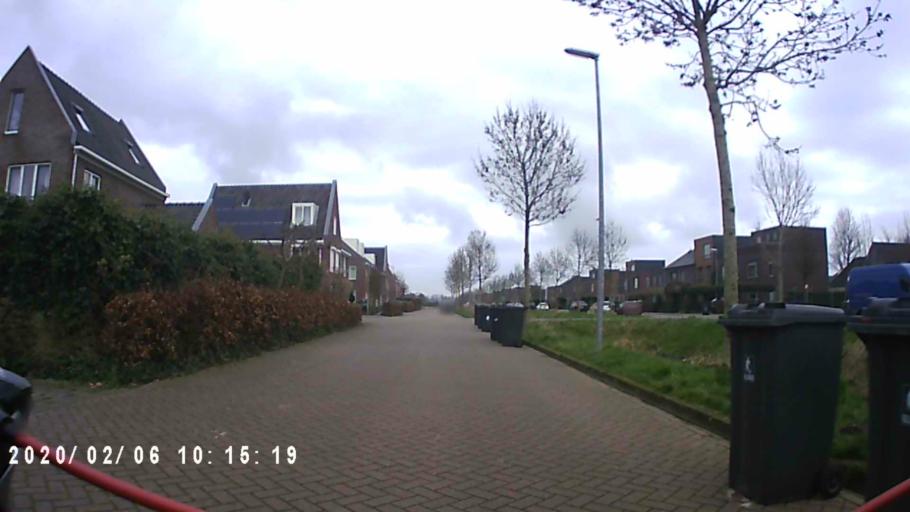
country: NL
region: Groningen
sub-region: Gemeente Groningen
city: Korrewegwijk
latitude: 53.2409
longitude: 6.5163
